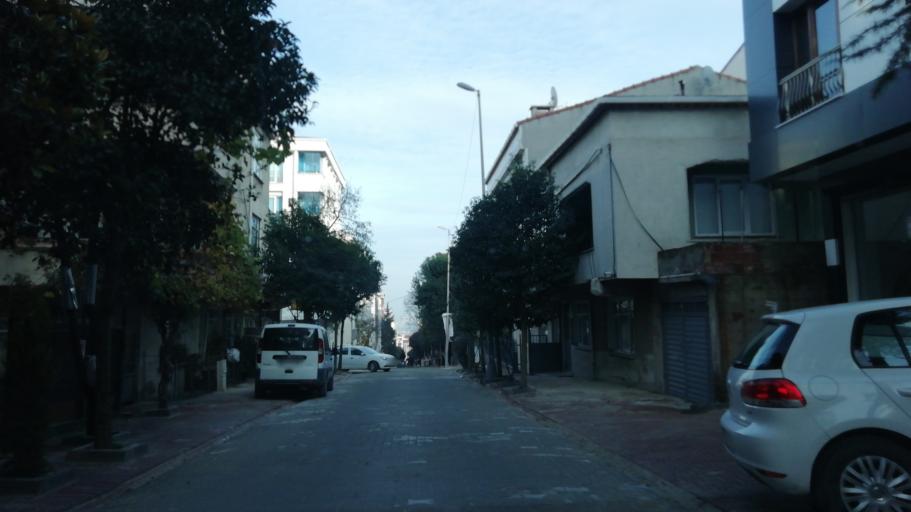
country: TR
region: Istanbul
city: Esenyurt
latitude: 41.0389
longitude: 28.6794
